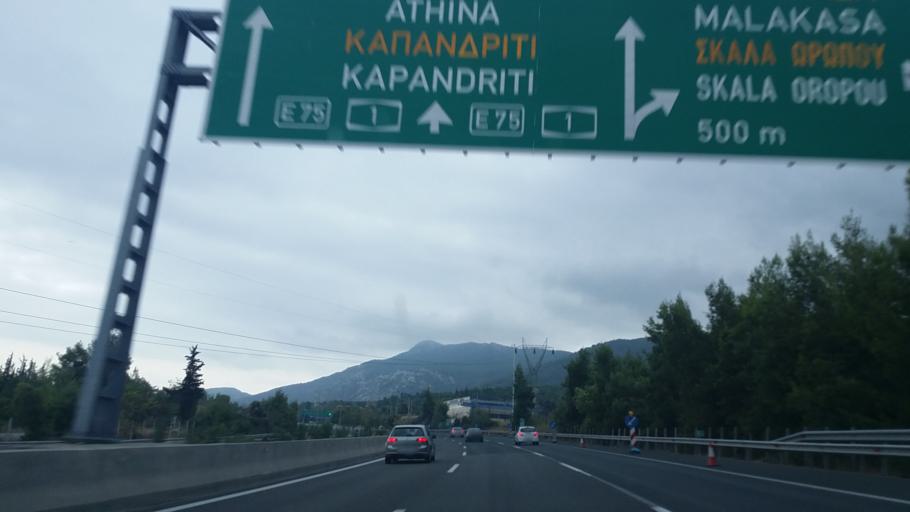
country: GR
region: Attica
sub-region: Nomarchia Anatolikis Attikis
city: Oropos
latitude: 38.2432
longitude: 23.7710
